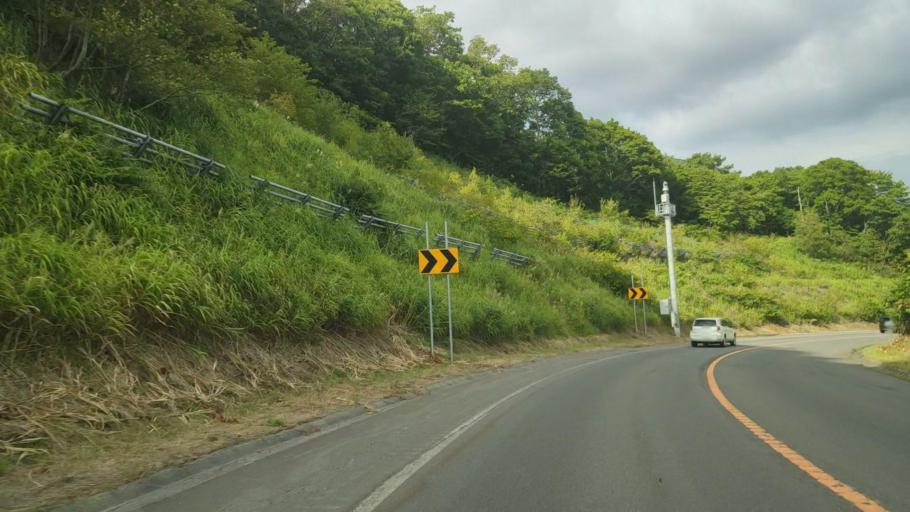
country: JP
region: Hokkaido
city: Ishikari
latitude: 43.4842
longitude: 141.3988
